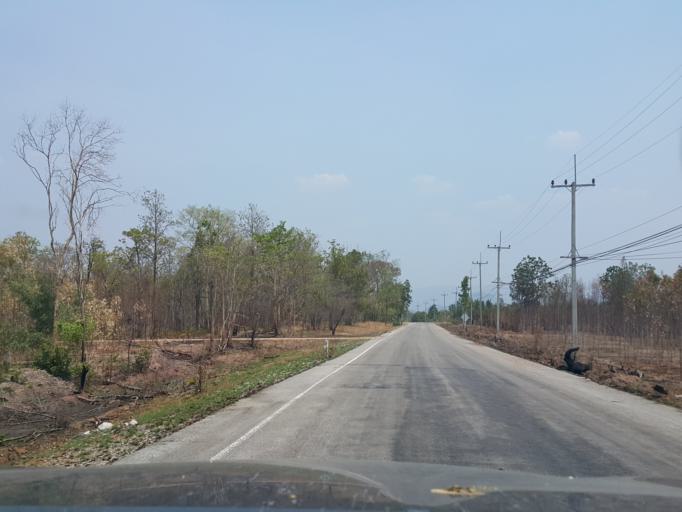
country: TH
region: Lampang
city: Mae Phrik
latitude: 17.5403
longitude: 99.1403
